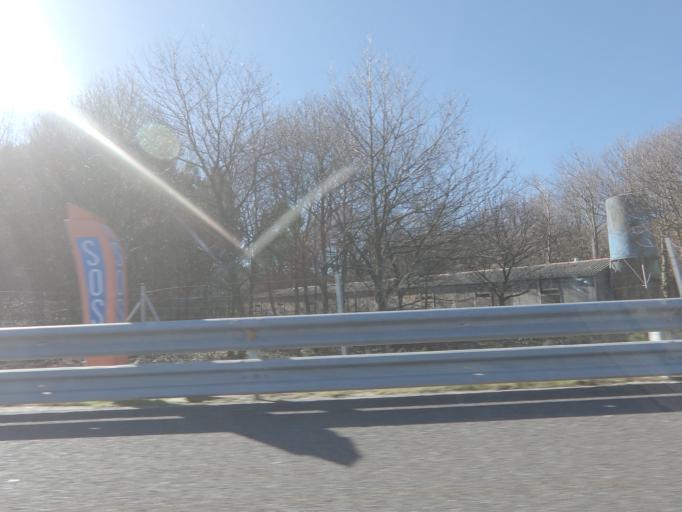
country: ES
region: Galicia
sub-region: Provincia de Pontevedra
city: Dozon
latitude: 42.5571
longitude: -8.0258
